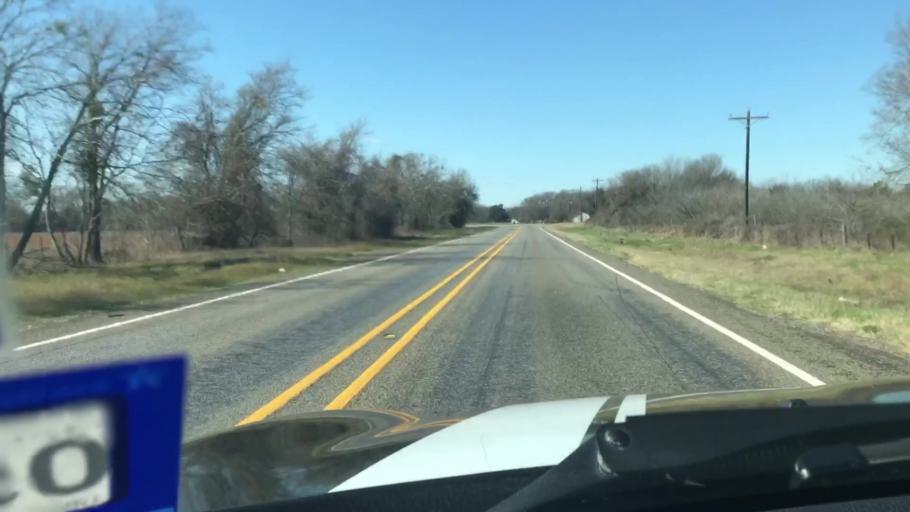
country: US
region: Texas
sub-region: Robertson County
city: Calvert
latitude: 30.8853
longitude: -96.7802
